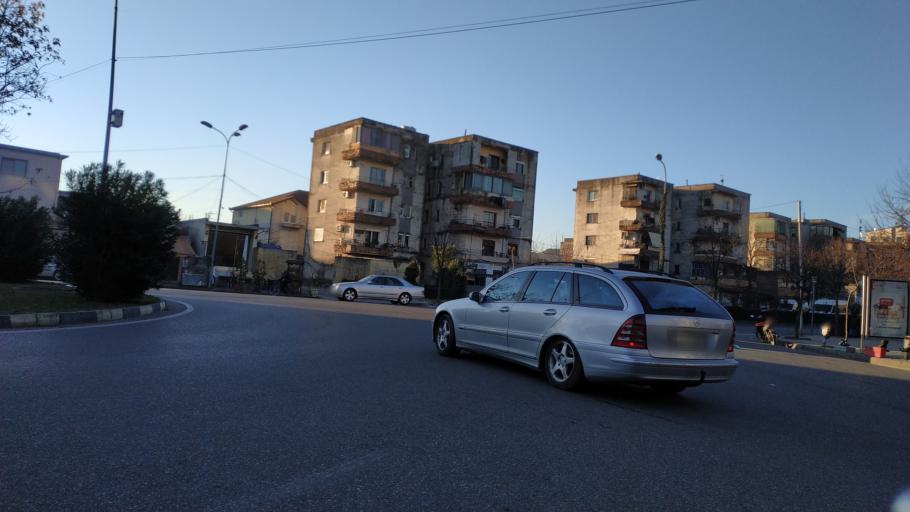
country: AL
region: Shkoder
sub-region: Rrethi i Shkodres
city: Shkoder
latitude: 42.0614
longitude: 19.5123
